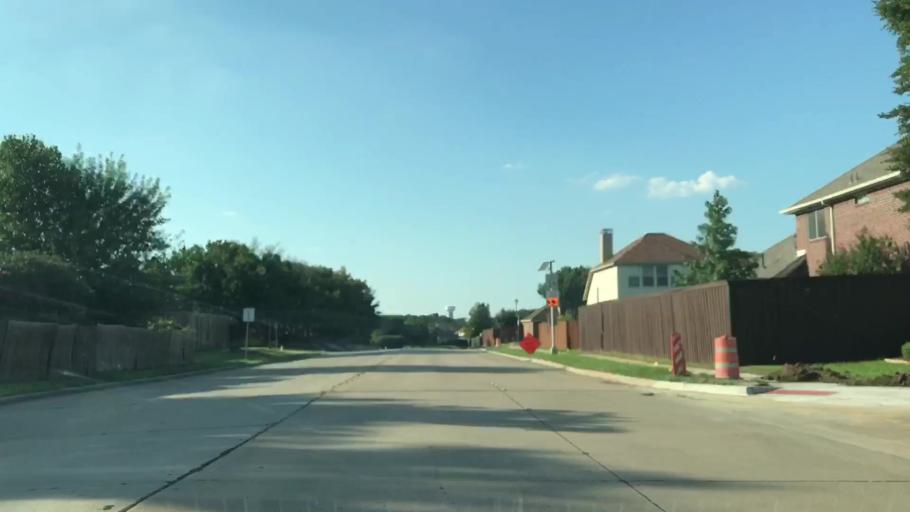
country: US
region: Texas
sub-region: Denton County
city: Lewisville
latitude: 33.0137
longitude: -97.0130
